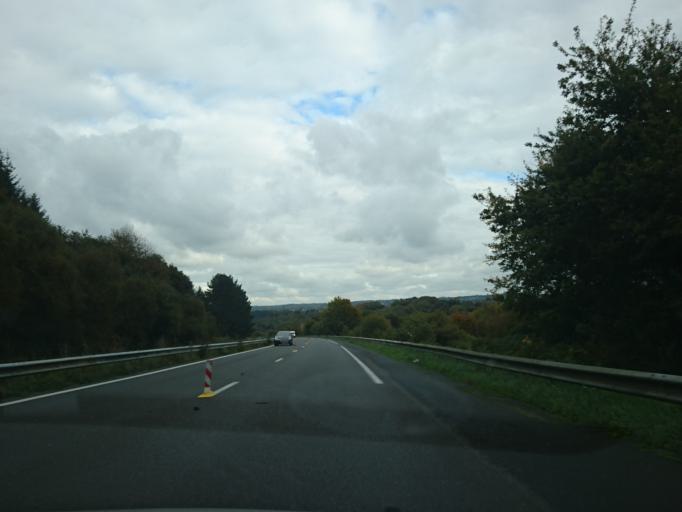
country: FR
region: Brittany
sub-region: Departement du Finistere
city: Plouigneau
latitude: 48.5720
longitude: -3.6673
